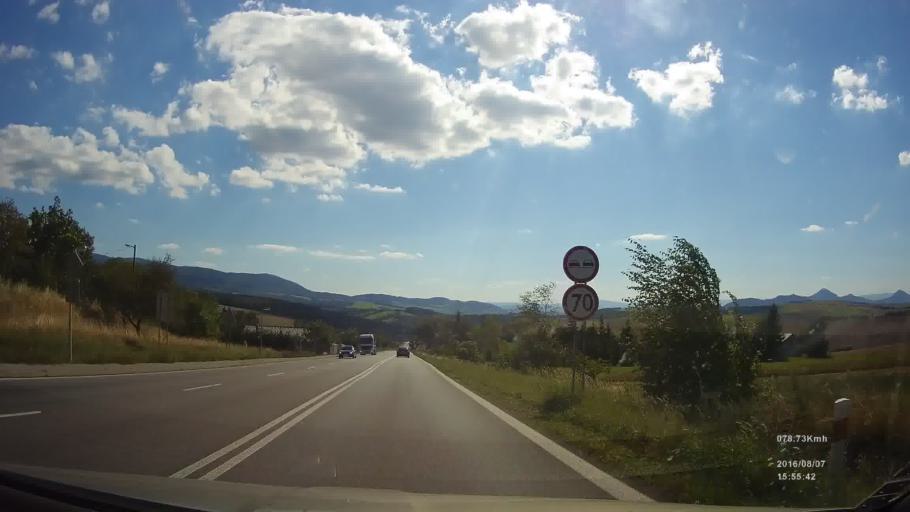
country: SK
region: Presovsky
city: Giraltovce
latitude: 49.0732
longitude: 21.4348
